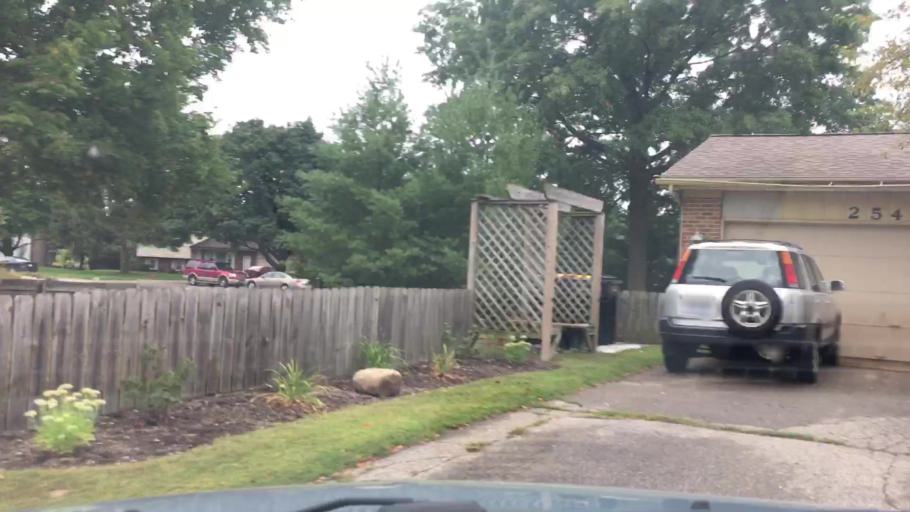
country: US
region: Michigan
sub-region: Ottawa County
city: Hudsonville
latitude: 42.9003
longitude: -85.8455
